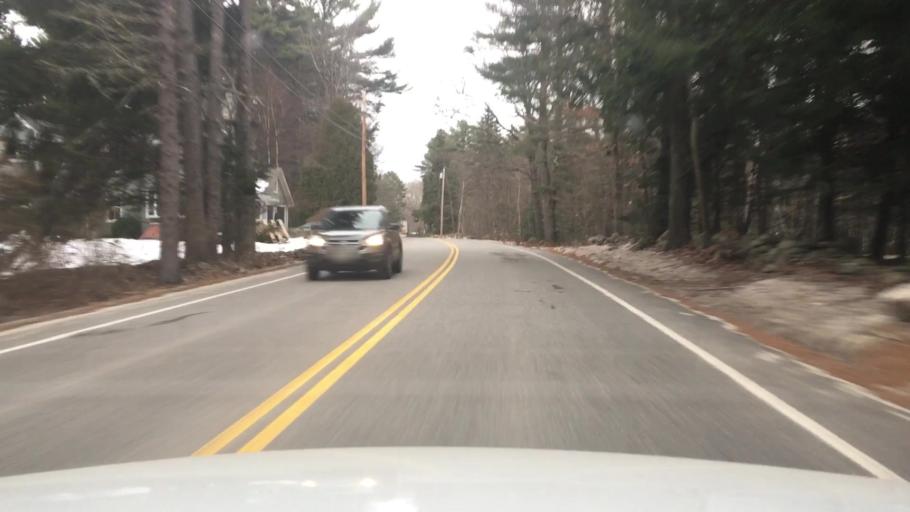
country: US
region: Maine
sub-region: Cumberland County
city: Freeport
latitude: 43.8641
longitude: -70.0706
